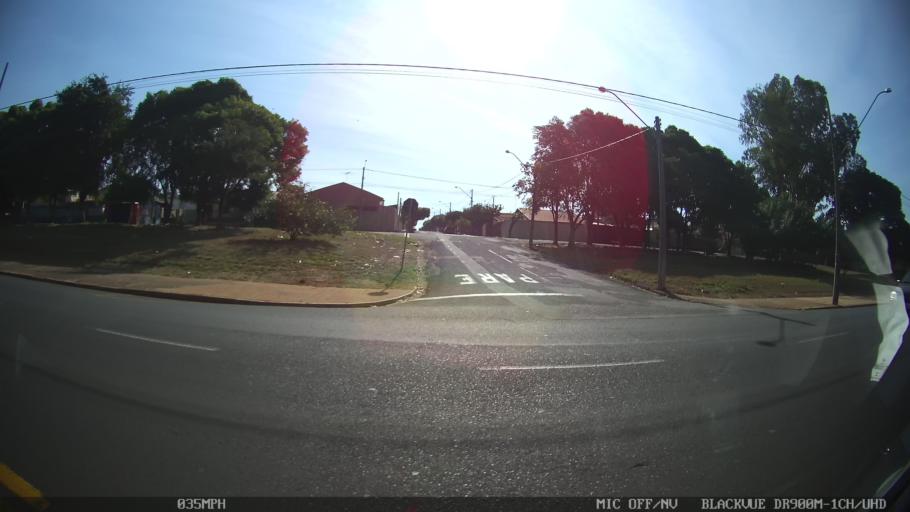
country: BR
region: Sao Paulo
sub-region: Sao Jose Do Rio Preto
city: Sao Jose do Rio Preto
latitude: -20.7938
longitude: -49.3950
